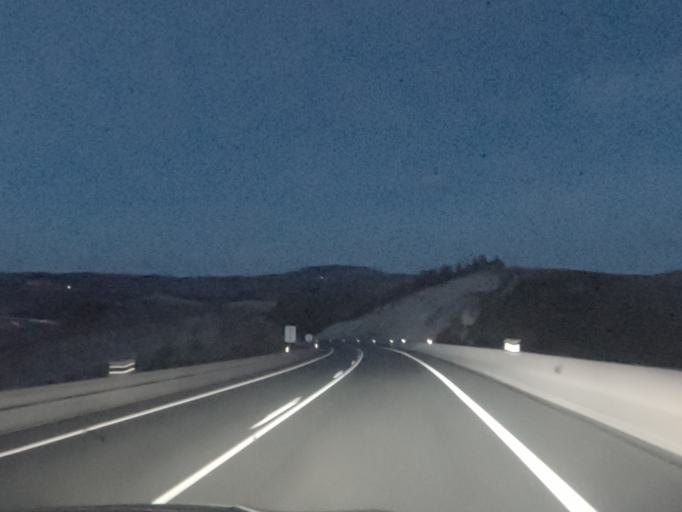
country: PT
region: Braganca
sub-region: Mogadouro
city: Mogadouro
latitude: 41.2722
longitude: -6.7451
